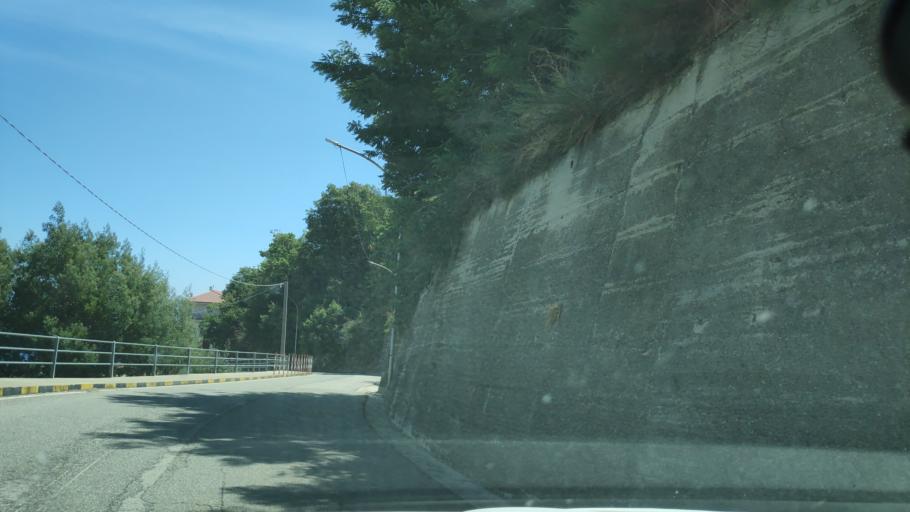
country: IT
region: Calabria
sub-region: Provincia di Catanzaro
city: Gasperina
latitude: 38.7386
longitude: 16.5101
